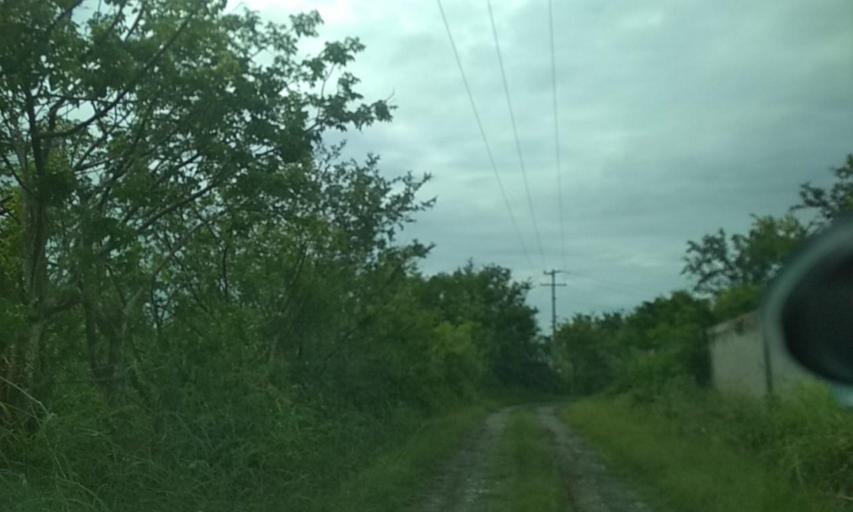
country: MX
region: Veracruz
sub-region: Cazones de Herrera
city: Rancho Nuevo
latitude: 20.6029
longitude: -97.1418
